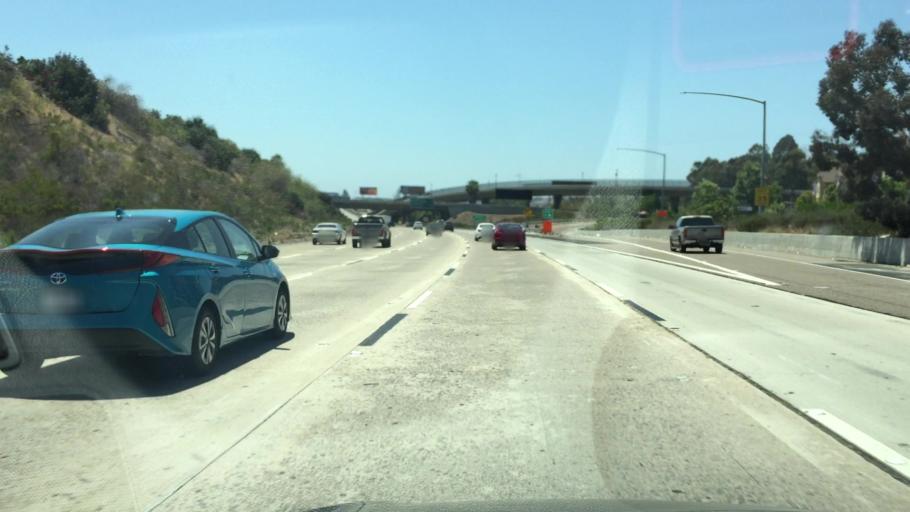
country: US
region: California
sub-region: San Diego County
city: La Mesa
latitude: 32.7811
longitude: -117.0846
